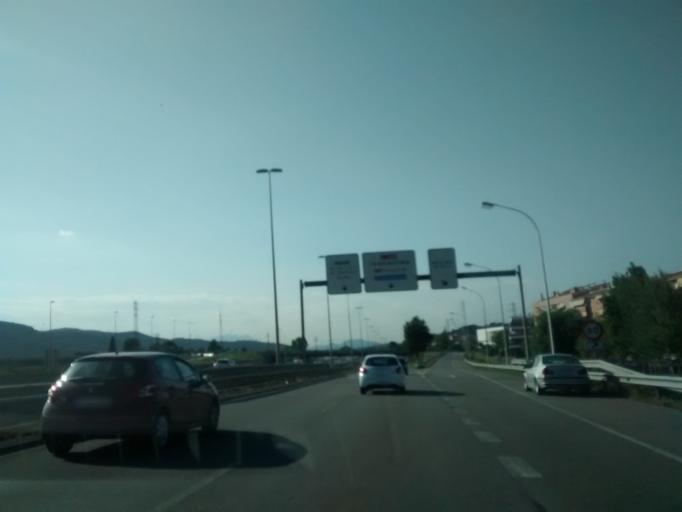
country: ES
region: Catalonia
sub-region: Provincia de Barcelona
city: Molins de Rei
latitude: 41.4067
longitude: 2.0162
